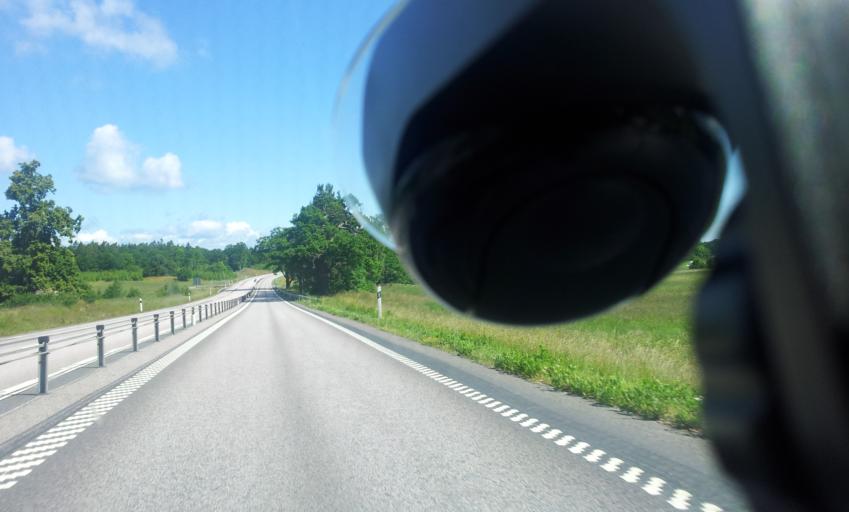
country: SE
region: Kalmar
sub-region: Monsteras Kommun
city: Moensteras
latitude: 57.0876
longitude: 16.4861
